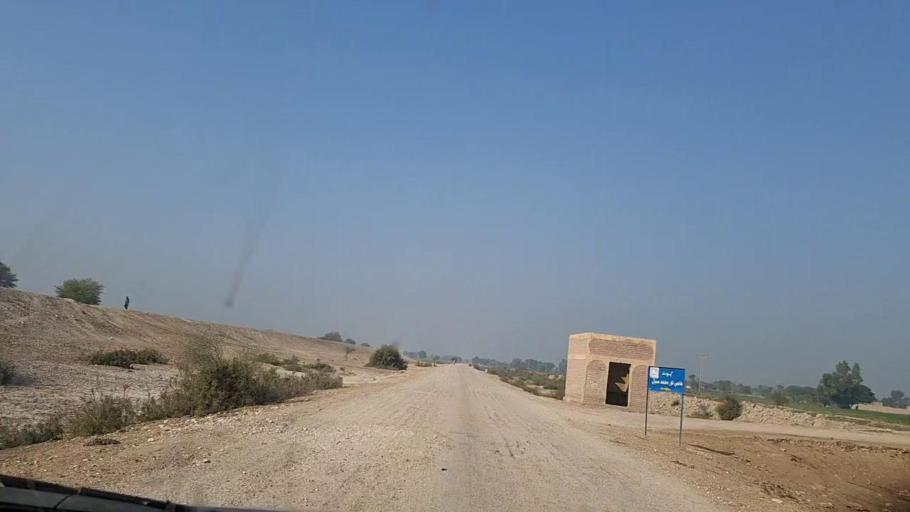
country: PK
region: Sindh
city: Moro
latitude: 26.7238
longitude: 67.9222
